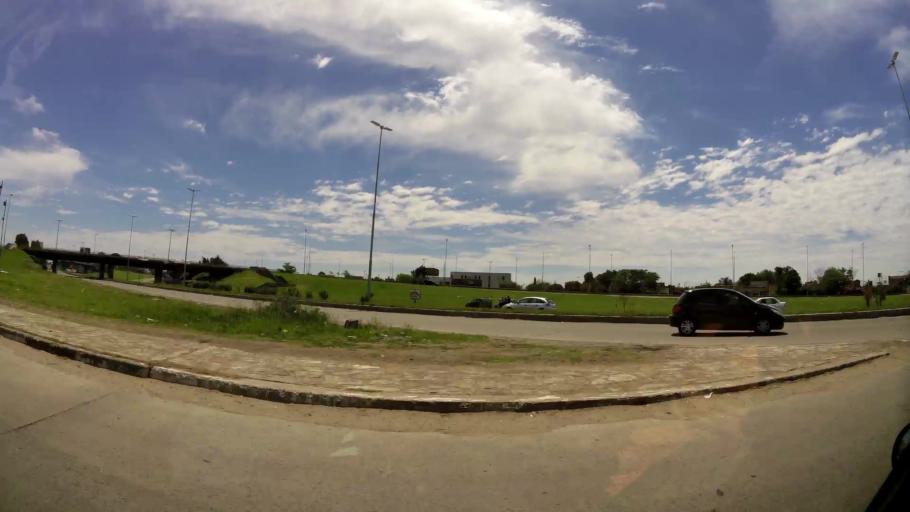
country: AR
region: Buenos Aires
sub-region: Partido de Quilmes
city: Quilmes
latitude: -34.7832
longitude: -58.2597
